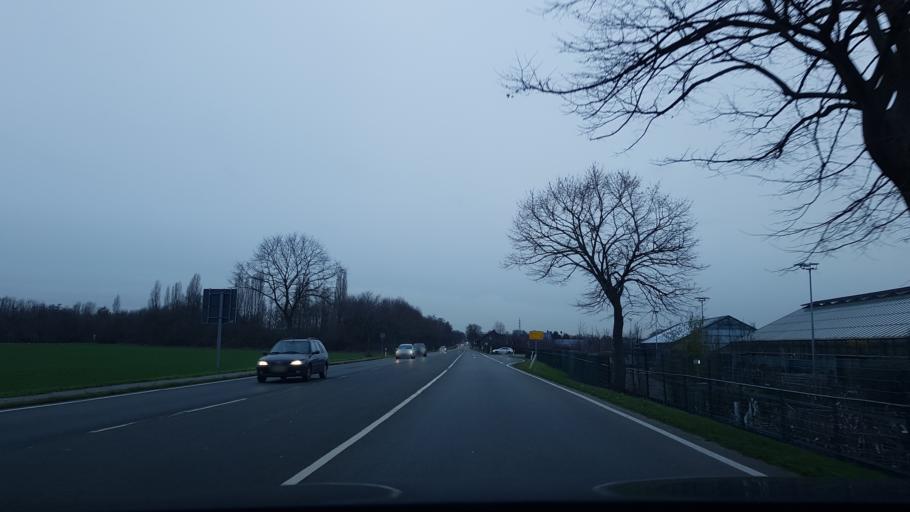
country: DE
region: North Rhine-Westphalia
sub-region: Regierungsbezirk Dusseldorf
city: Moers
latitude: 51.4115
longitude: 6.6613
